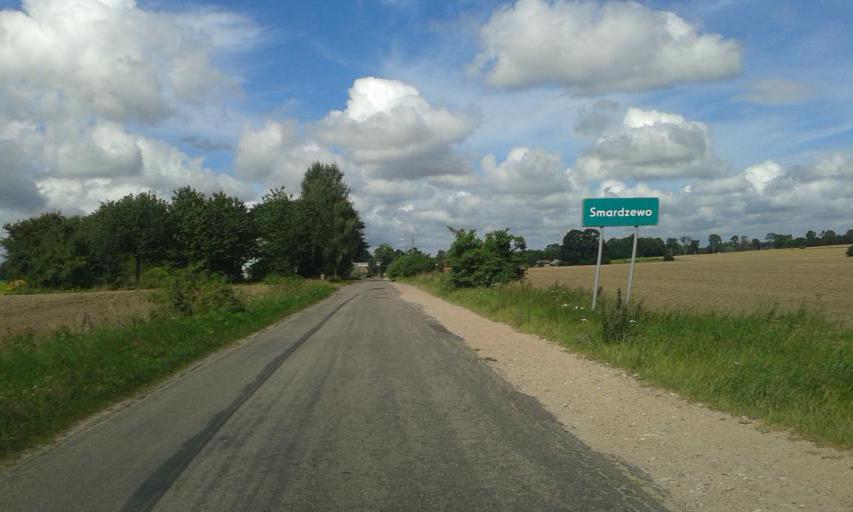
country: PL
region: West Pomeranian Voivodeship
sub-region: Powiat slawienski
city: Slawno
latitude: 54.3000
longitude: 16.6361
